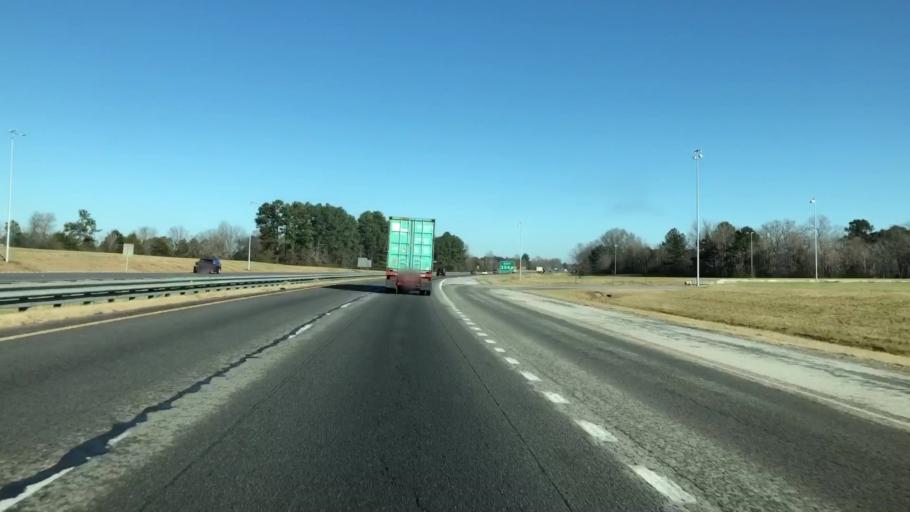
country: US
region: Alabama
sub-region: Limestone County
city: Athens
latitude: 34.8301
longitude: -86.9386
